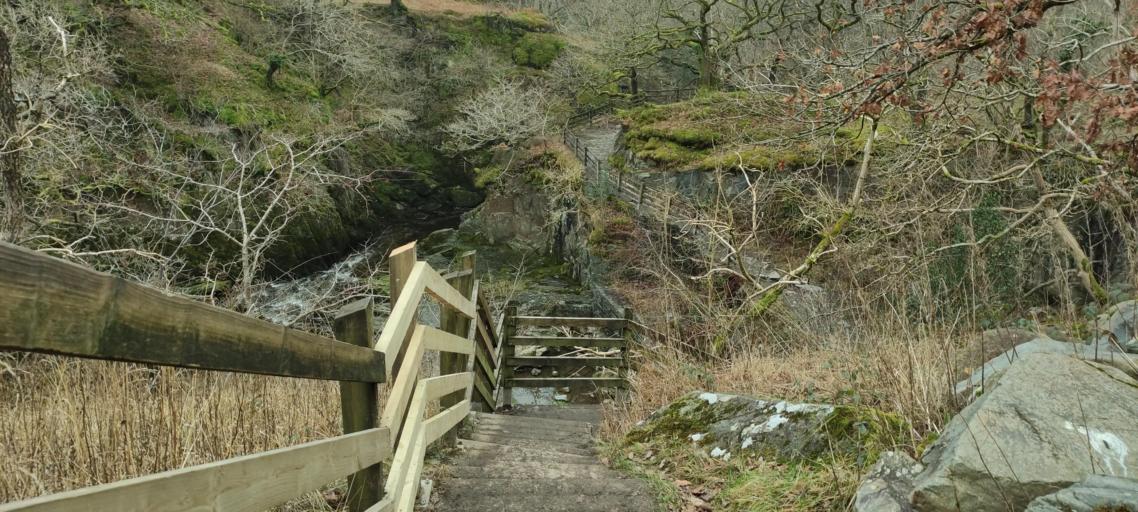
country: GB
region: England
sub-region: North Yorkshire
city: Ingleton
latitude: 54.1648
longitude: -2.4551
